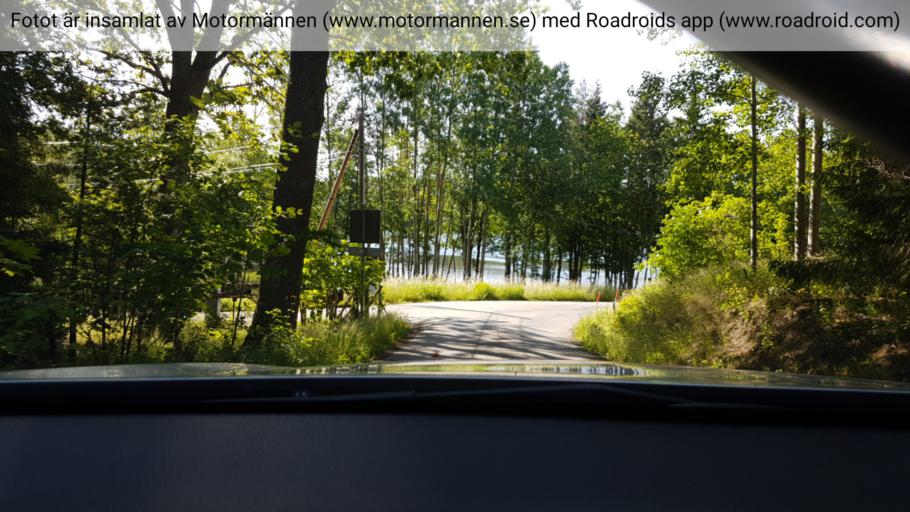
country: SE
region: Stockholm
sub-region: Haninge Kommun
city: Jordbro
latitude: 59.0175
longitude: 18.1147
